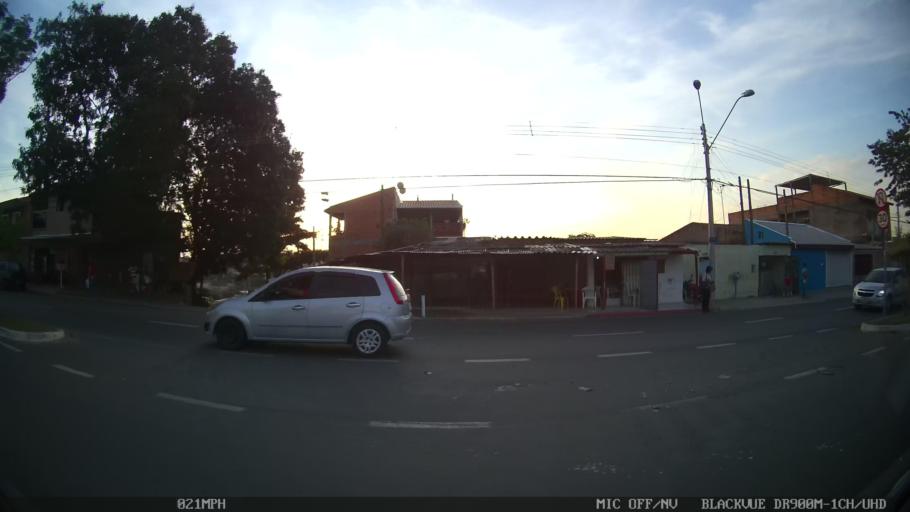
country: BR
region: Sao Paulo
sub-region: Campinas
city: Campinas
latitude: -22.9755
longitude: -47.1365
